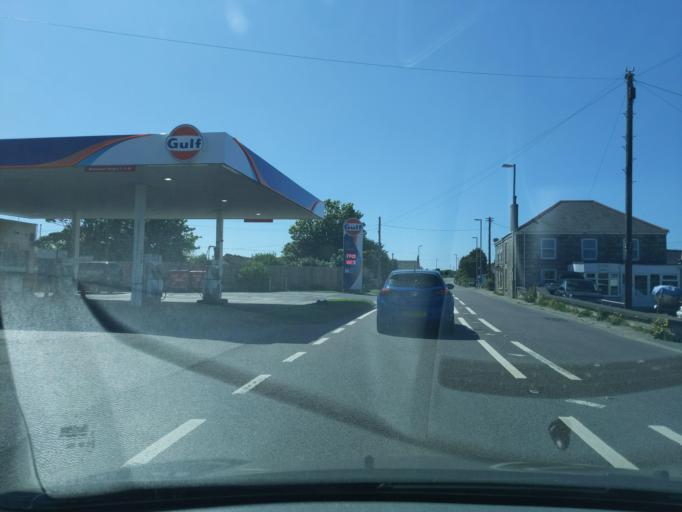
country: GB
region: England
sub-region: Cornwall
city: Penryn
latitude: 50.1639
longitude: -5.1580
